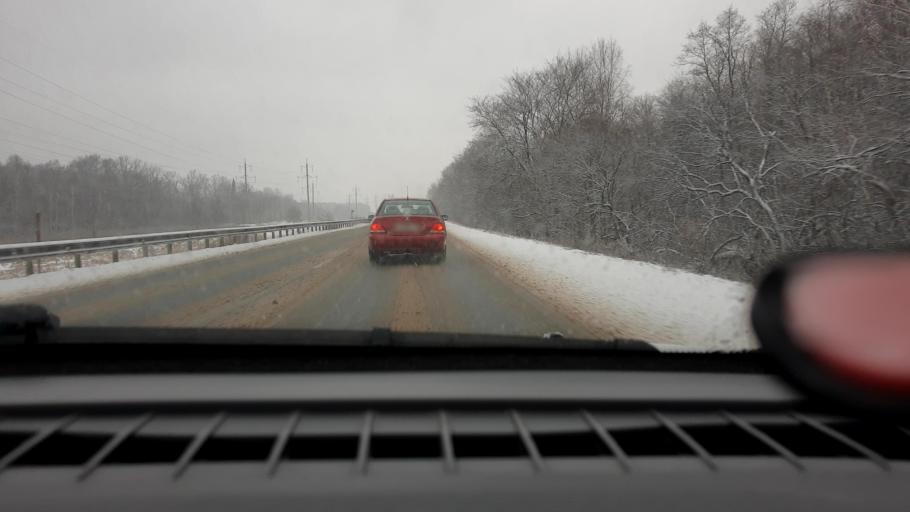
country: RU
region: Nizjnij Novgorod
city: Lukino
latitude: 56.4607
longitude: 43.6224
